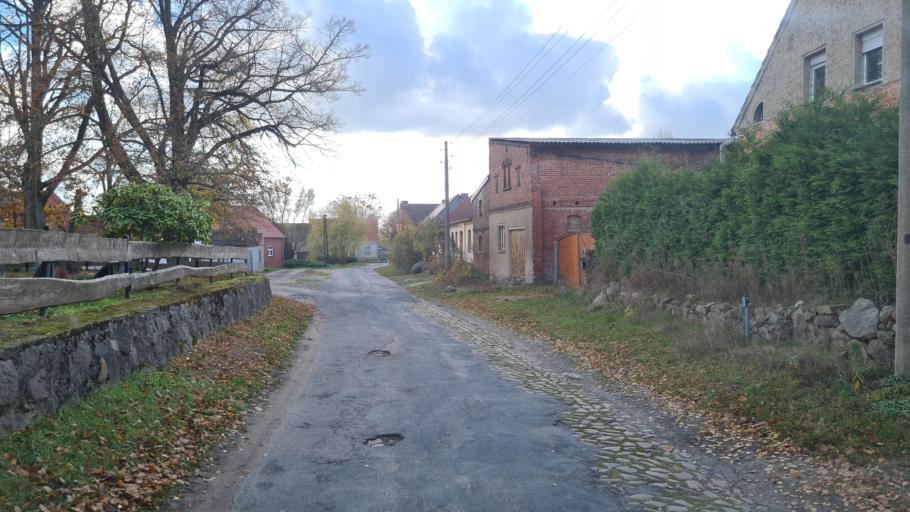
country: DE
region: Saxony-Anhalt
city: Kropstadt
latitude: 52.0082
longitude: 12.7229
